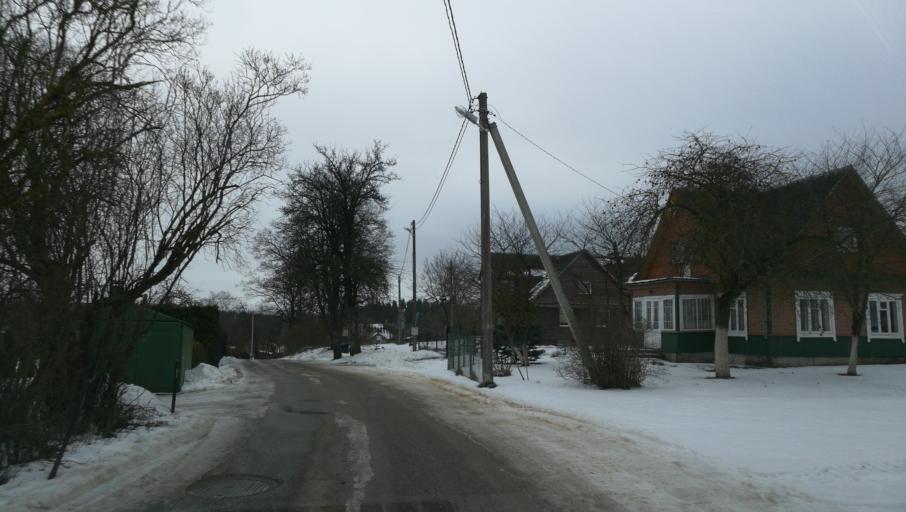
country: LT
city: Trakai
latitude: 54.6160
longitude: 24.9216
